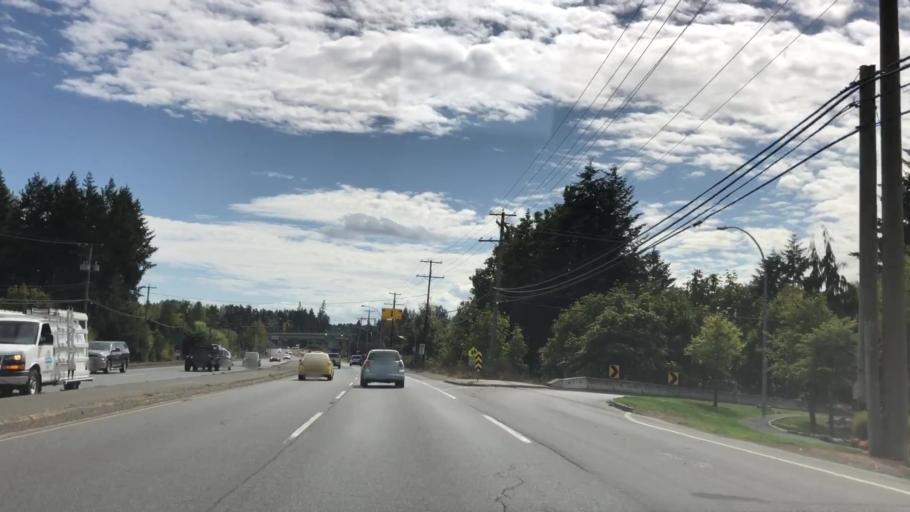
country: CA
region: British Columbia
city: Nanaimo
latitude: 49.1295
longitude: -123.9210
